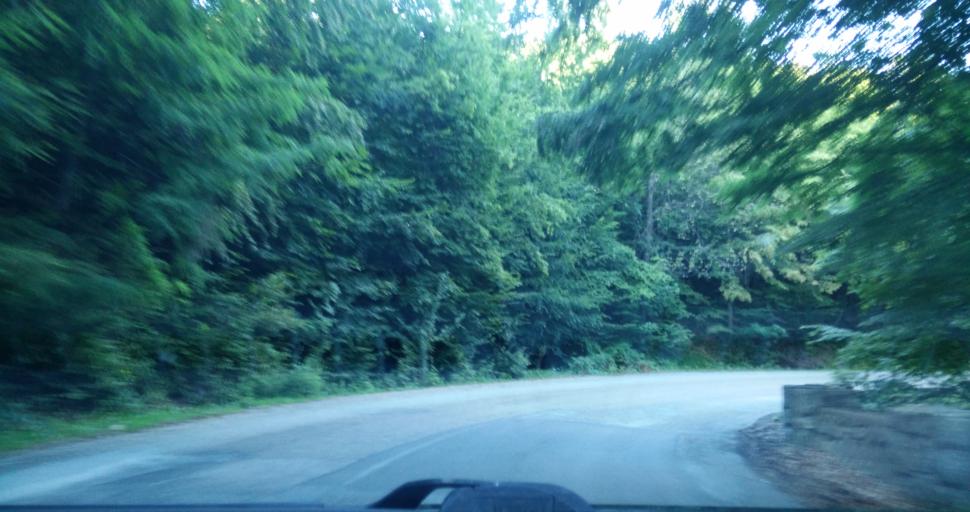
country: RO
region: Bihor
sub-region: Oras Nucet
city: Nucet
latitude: 46.4929
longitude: 22.6060
